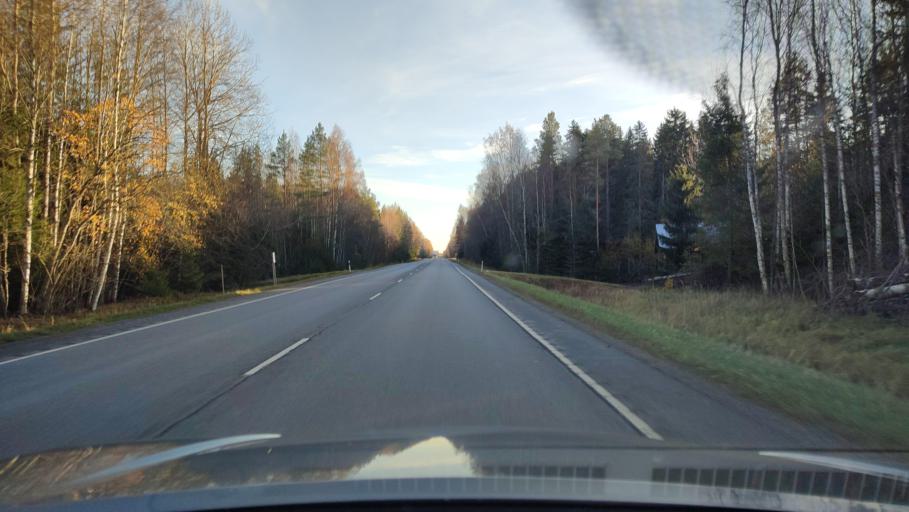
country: FI
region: Ostrobothnia
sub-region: Vaasa
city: Ristinummi
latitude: 63.0046
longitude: 21.7634
